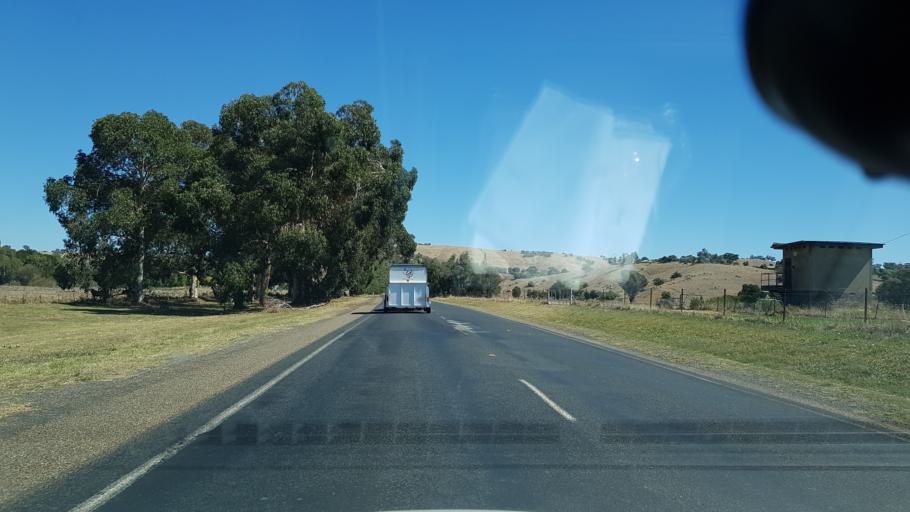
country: AU
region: New South Wales
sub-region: Gundagai
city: Gundagai
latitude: -34.8228
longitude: 148.3372
